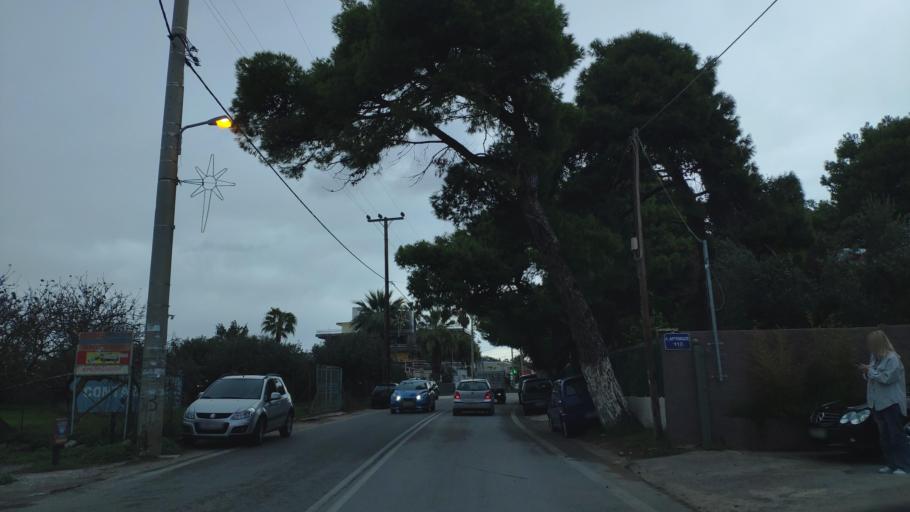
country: GR
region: Attica
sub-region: Nomarchia Anatolikis Attikis
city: Artemida
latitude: 37.9785
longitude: 24.0081
